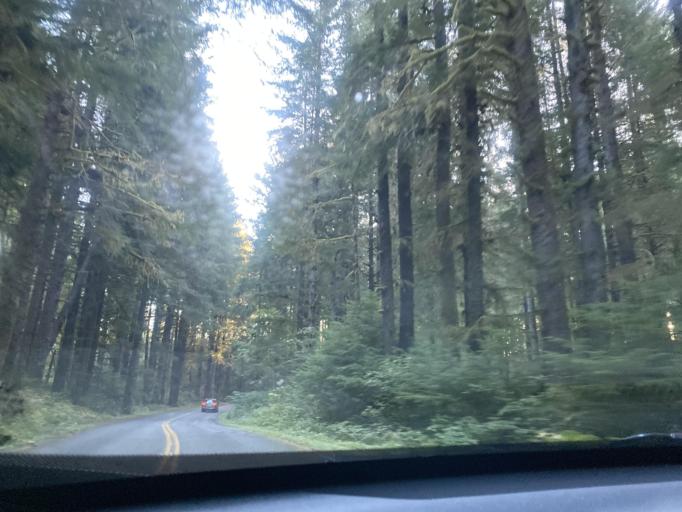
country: US
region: Washington
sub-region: Clallam County
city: Forks
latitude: 47.8091
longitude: -124.1004
